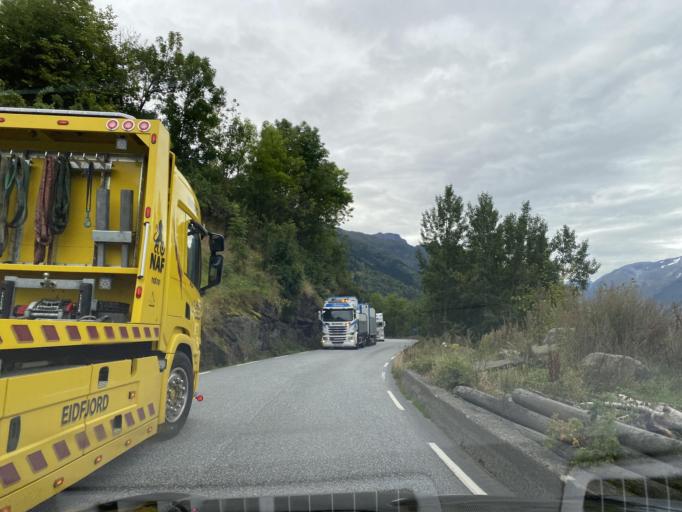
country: NO
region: Hordaland
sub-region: Odda
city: Odda
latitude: 60.2166
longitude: 6.6026
